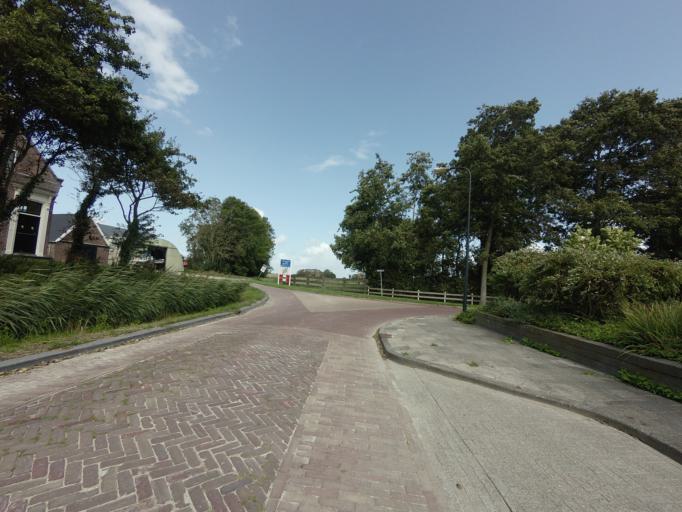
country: NL
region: Friesland
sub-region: Gemeente Harlingen
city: Harlingen
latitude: 53.1173
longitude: 5.4380
